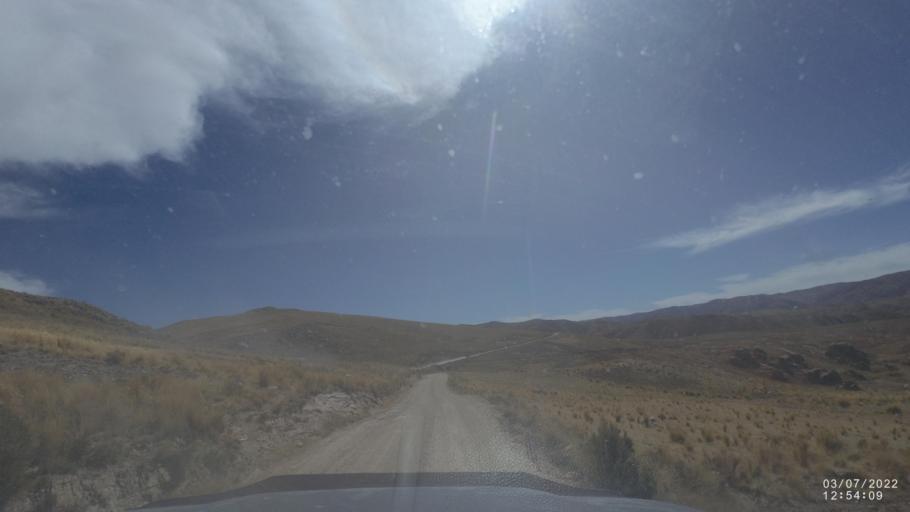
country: BO
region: Cochabamba
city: Irpa Irpa
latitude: -17.7406
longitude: -66.6669
